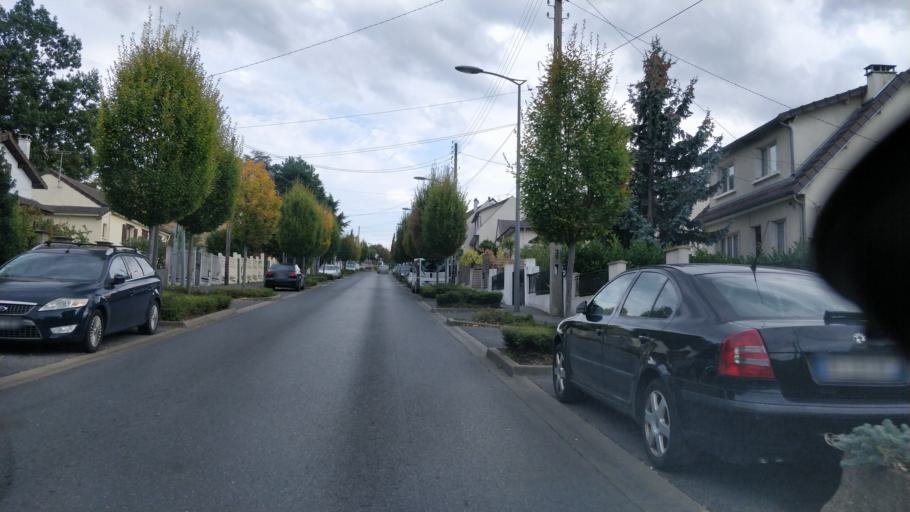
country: FR
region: Ile-de-France
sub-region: Departement de Seine-Saint-Denis
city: Livry-Gargan
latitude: 48.9162
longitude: 2.5477
